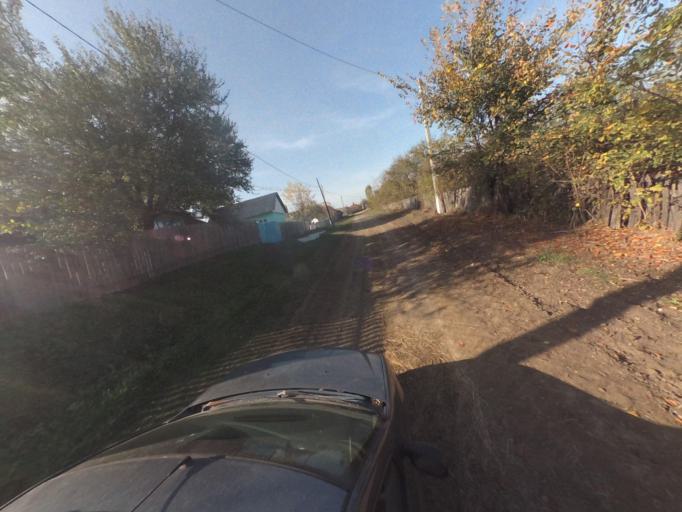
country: RO
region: Vaslui
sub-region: Comuna Bacesti
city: Bacesti
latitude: 46.8729
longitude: 27.1975
